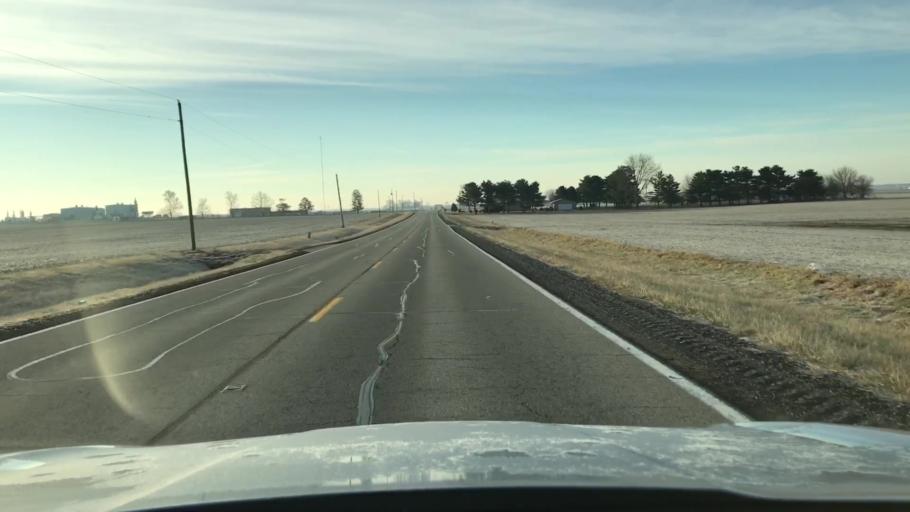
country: US
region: Illinois
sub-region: McLean County
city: Hudson
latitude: 40.5885
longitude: -88.9448
